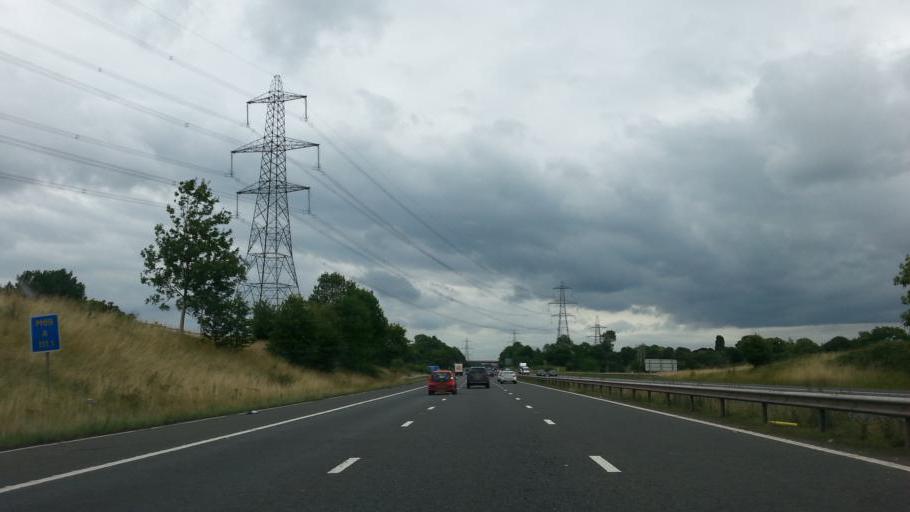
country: GB
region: England
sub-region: Leicestershire
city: Hinckley
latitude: 52.5186
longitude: -1.3503
